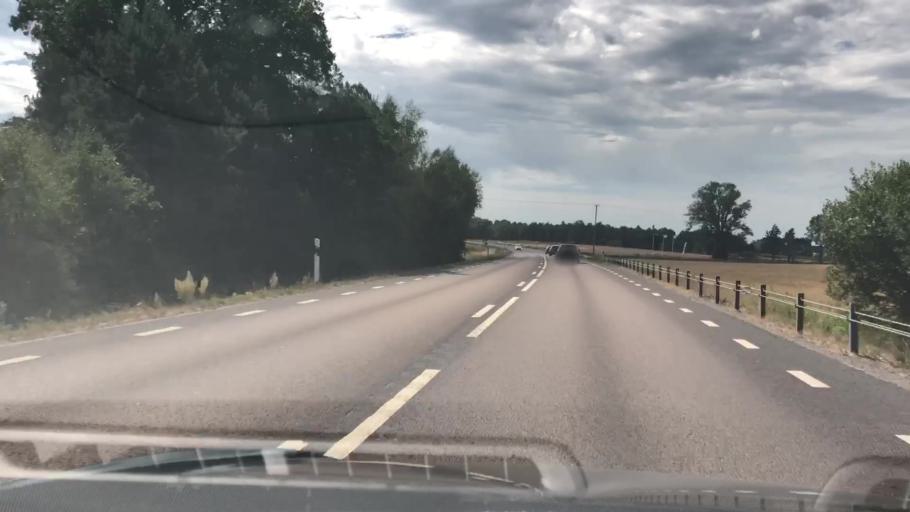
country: SE
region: Kalmar
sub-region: Torsas Kommun
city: Torsas
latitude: 56.3688
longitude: 16.0648
